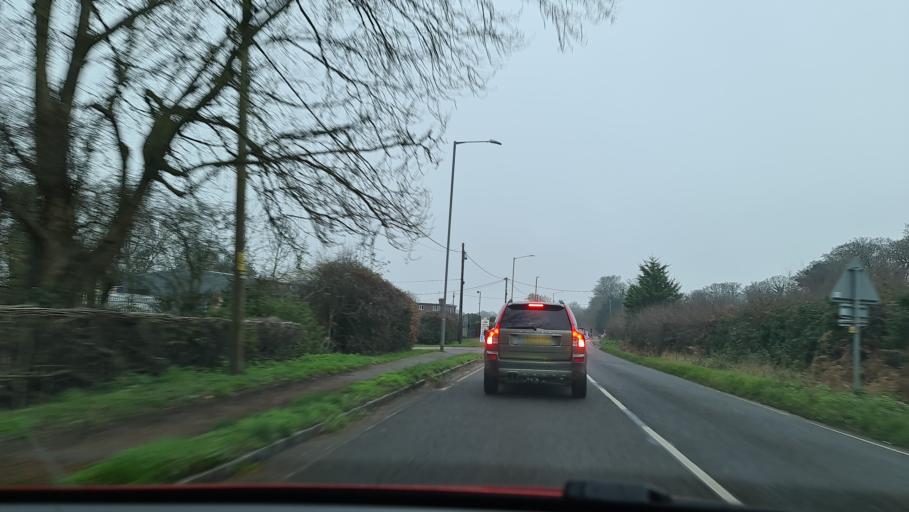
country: GB
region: England
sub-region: Buckinghamshire
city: Stokenchurch
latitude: 51.6499
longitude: -0.8606
